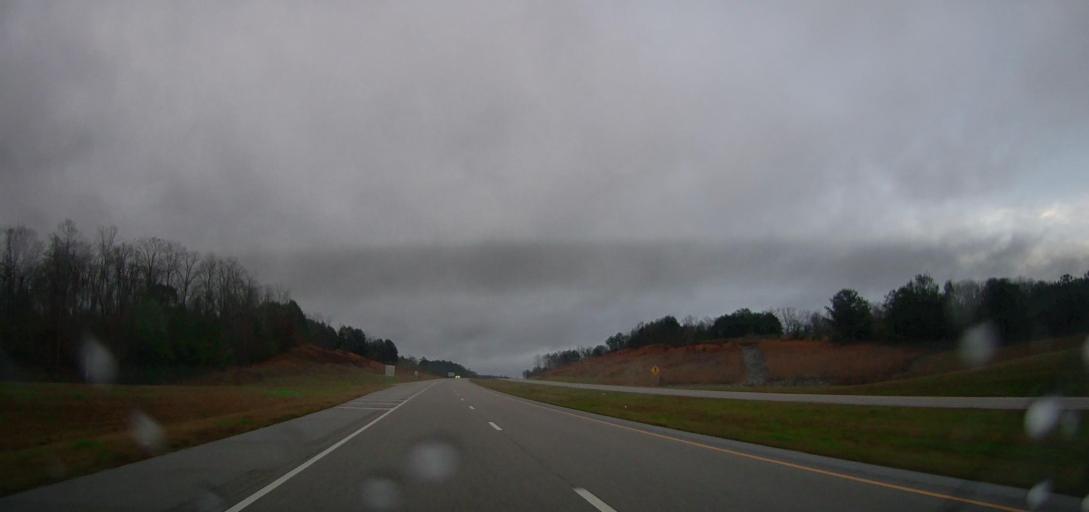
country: US
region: Alabama
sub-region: Bibb County
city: Centreville
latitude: 32.9574
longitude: -87.1322
